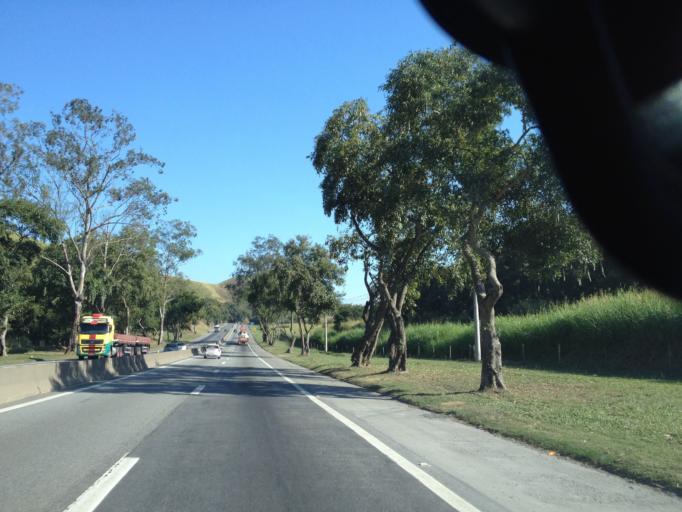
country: BR
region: Rio de Janeiro
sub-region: Porto Real
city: Porto Real
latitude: -22.4747
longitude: -44.2694
